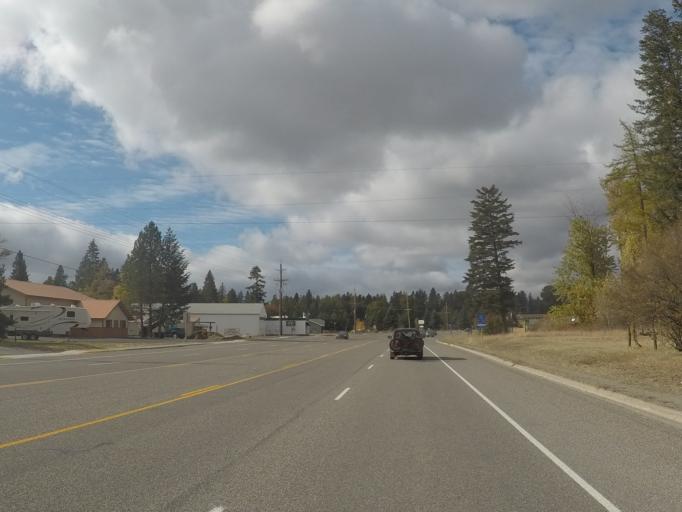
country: US
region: Montana
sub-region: Flathead County
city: Columbia Falls
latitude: 48.3668
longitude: -114.1726
